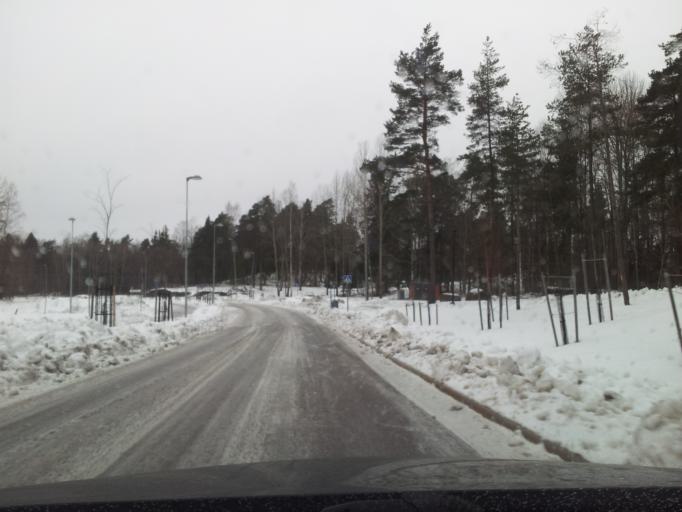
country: FI
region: Uusimaa
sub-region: Helsinki
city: Espoo
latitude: 60.1601
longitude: 24.5605
